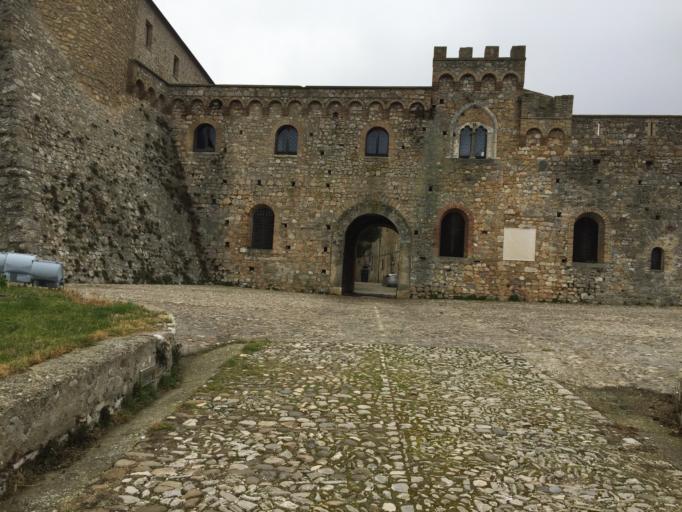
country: IT
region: Apulia
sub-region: Provincia di Foggia
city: Bovino
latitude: 41.2515
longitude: 15.3390
